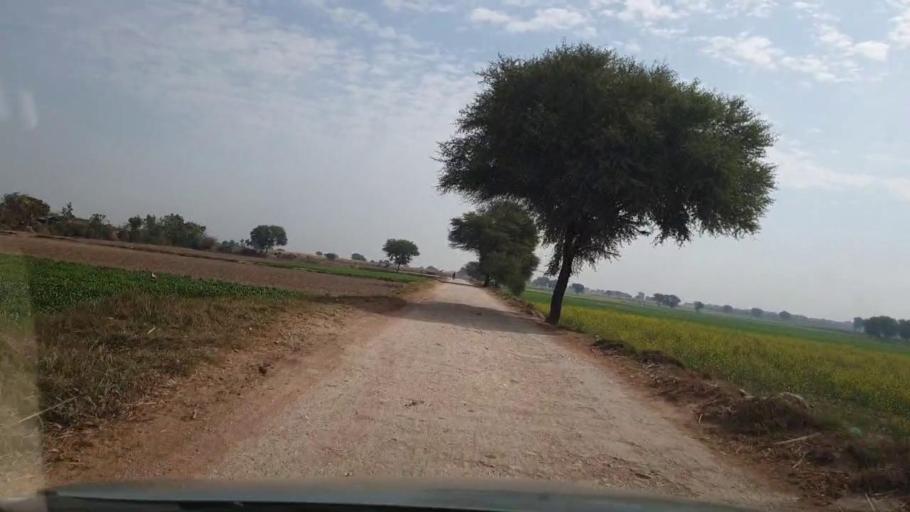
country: PK
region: Sindh
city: Tando Jam
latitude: 25.5212
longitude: 68.5549
